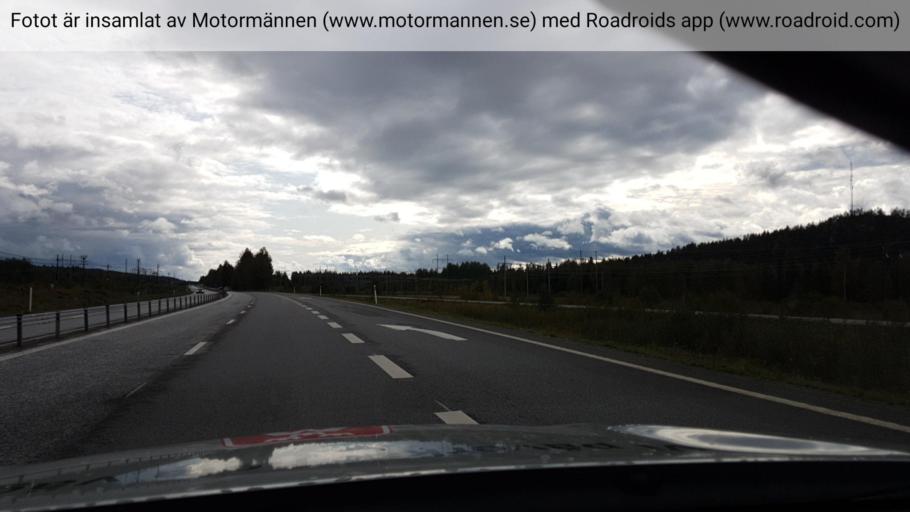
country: SE
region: Norrbotten
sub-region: Bodens Kommun
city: Saevast
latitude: 65.7867
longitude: 21.7369
